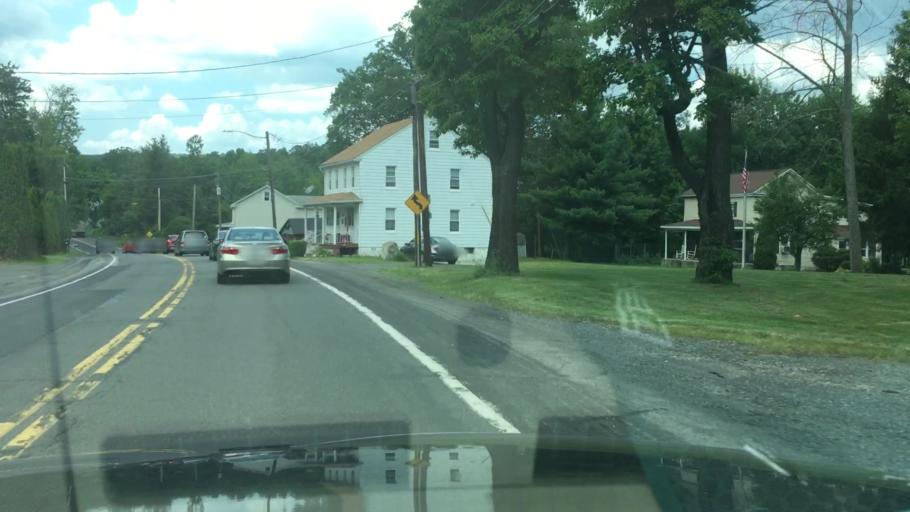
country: US
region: Pennsylvania
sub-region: Schuylkill County
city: Minersville
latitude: 40.7025
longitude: -76.3253
